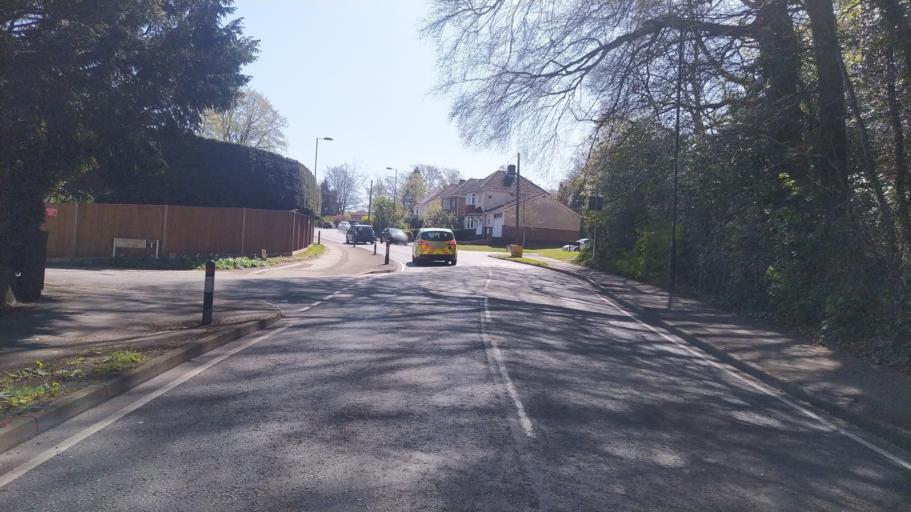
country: GB
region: England
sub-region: Southampton
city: Southampton
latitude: 50.9370
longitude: -1.4223
